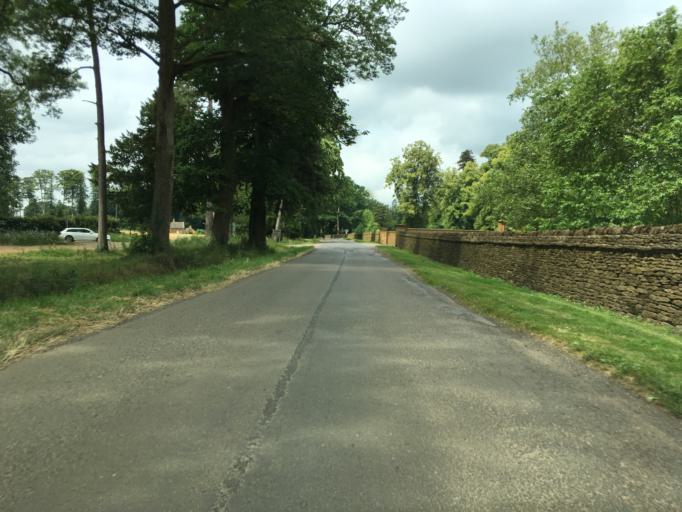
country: GB
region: England
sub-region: Oxfordshire
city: Hook Norton
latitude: 51.9550
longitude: -1.4168
